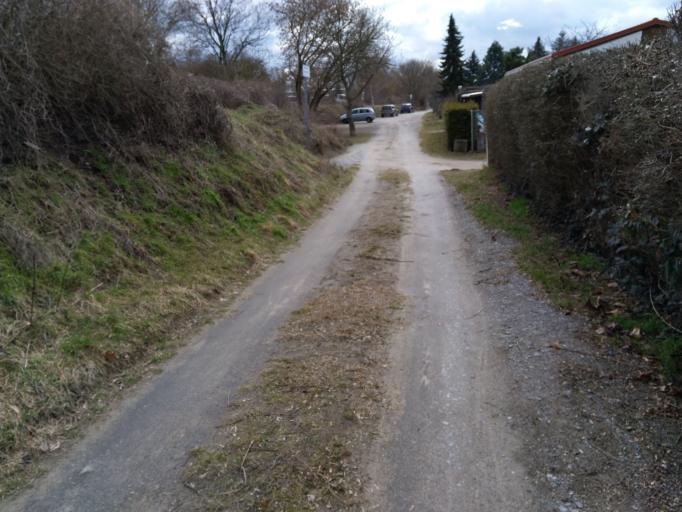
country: DE
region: Berlin
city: Karlshorst
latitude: 52.4864
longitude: 13.5462
